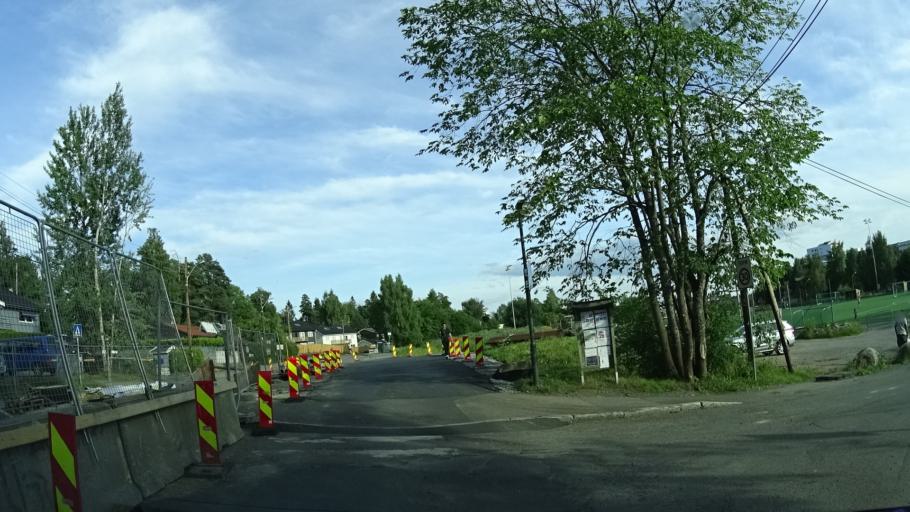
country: NO
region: Oslo
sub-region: Oslo
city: Sjolyststranda
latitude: 59.9555
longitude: 10.6558
